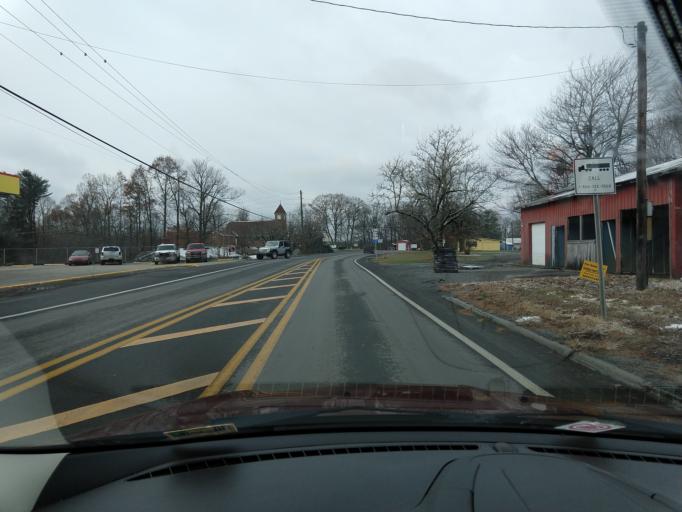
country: US
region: West Virginia
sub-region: Nicholas County
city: Craigsville
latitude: 38.2256
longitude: -80.6911
